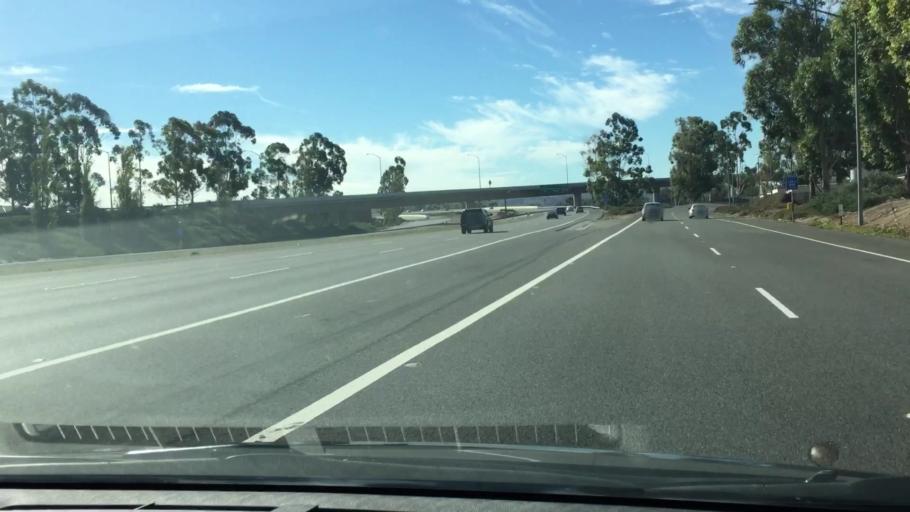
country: US
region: California
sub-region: Orange County
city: Lake Forest
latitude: 33.6792
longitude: -117.7510
